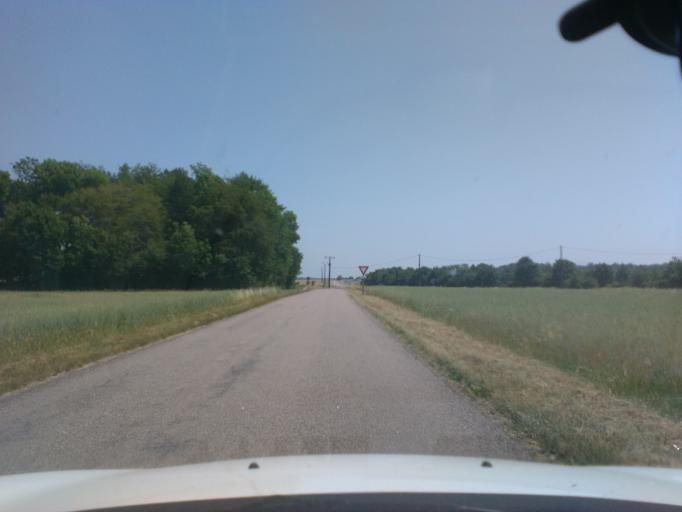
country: FR
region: Lorraine
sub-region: Departement des Vosges
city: Neufchateau
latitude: 48.3539
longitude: 5.7220
